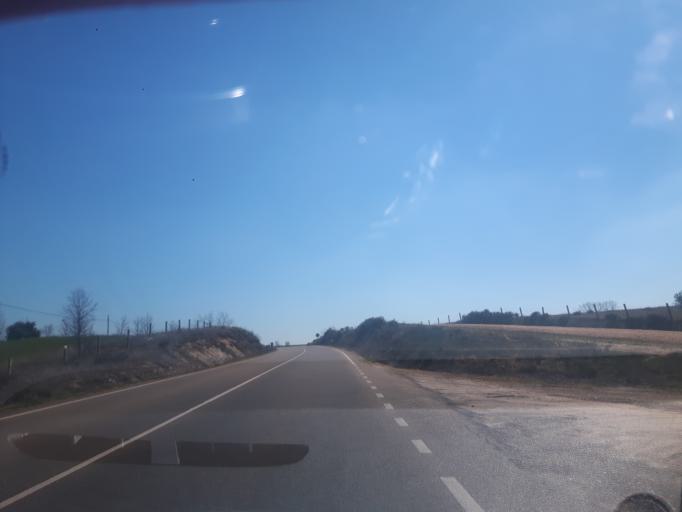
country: ES
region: Castille and Leon
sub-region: Provincia de Salamanca
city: Peralejos de Abajo
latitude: 41.0058
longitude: -6.3886
